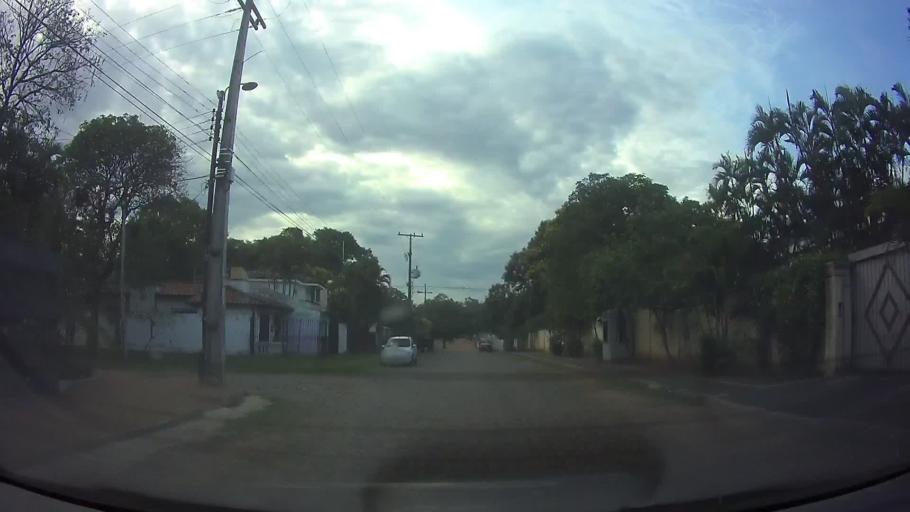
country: PY
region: Central
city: Fernando de la Mora
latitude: -25.2739
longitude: -57.5584
